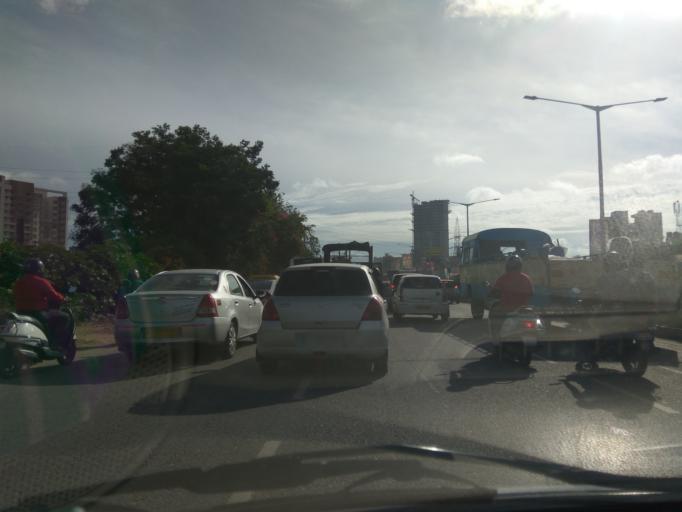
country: IN
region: Karnataka
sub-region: Bangalore Rural
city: Hoskote
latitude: 13.0161
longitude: 77.7022
